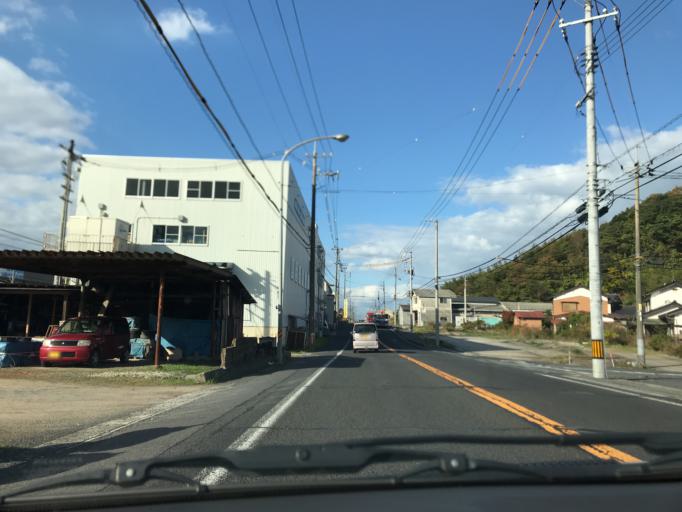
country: JP
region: Shimane
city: Yasugicho
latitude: 35.4280
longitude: 133.2710
